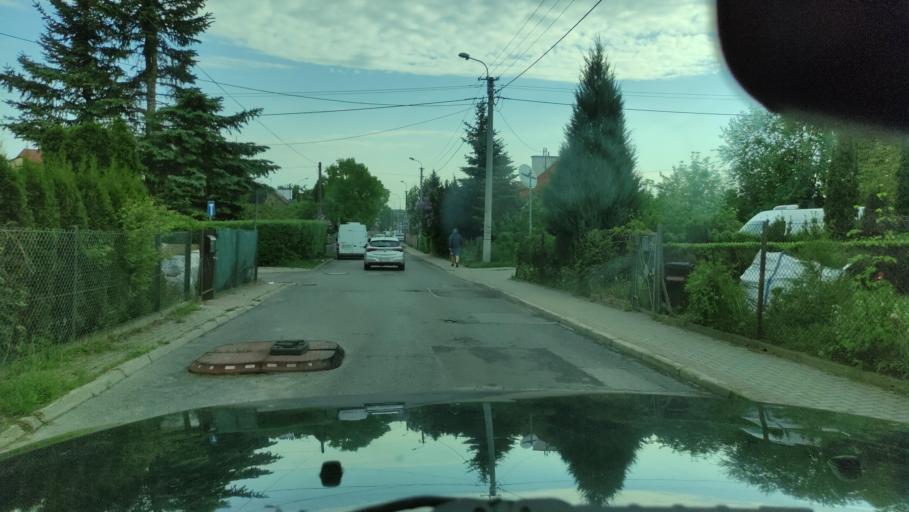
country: PL
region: Warmian-Masurian Voivodeship
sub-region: Powiat olsztynski
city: Olsztyn
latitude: 53.7647
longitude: 20.5083
